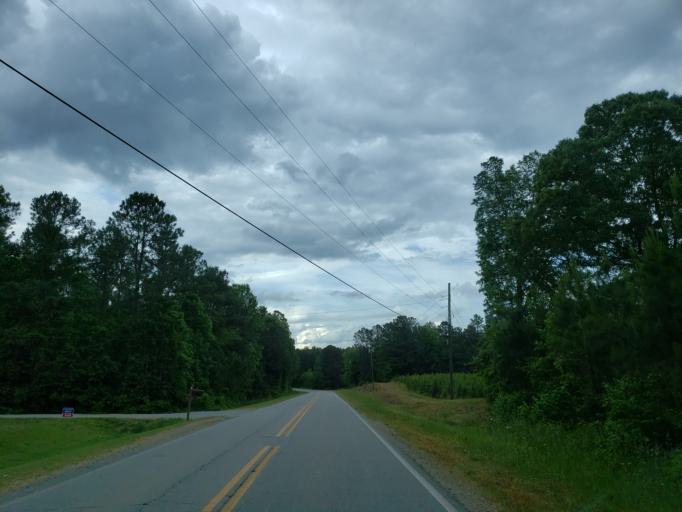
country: US
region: Georgia
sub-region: Polk County
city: Rockmart
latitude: 33.9103
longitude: -85.0632
